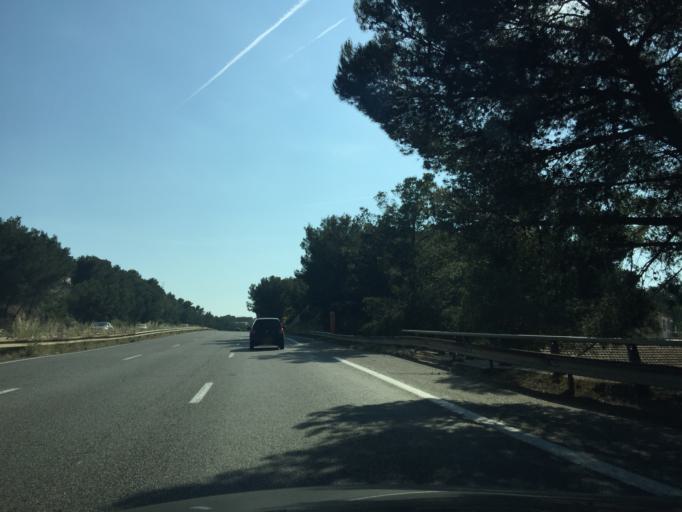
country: FR
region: Provence-Alpes-Cote d'Azur
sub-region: Departement des Bouches-du-Rhone
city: Martigues
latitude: 43.3964
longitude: 5.0696
